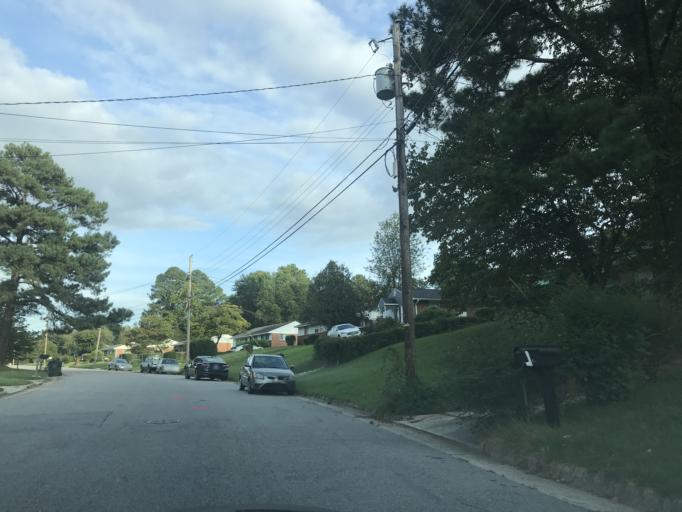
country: US
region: North Carolina
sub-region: Wake County
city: Raleigh
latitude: 35.7498
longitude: -78.6264
